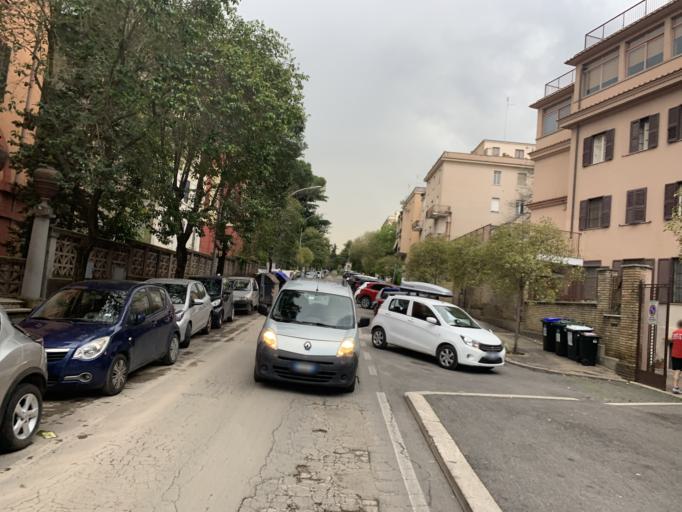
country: VA
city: Vatican City
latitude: 41.8851
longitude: 12.4582
